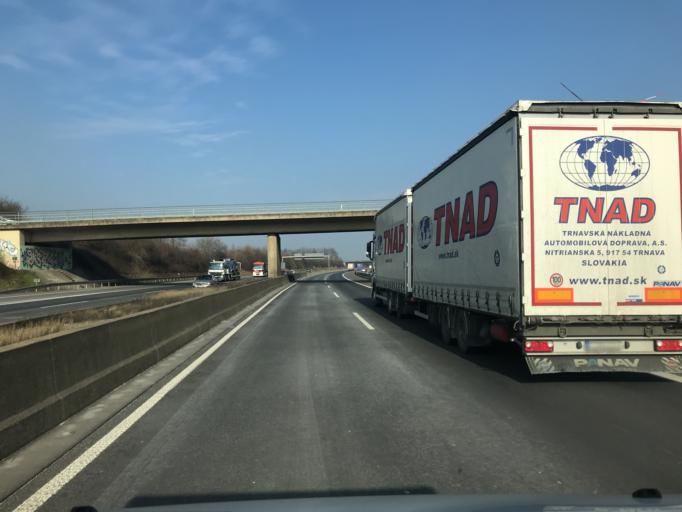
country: DE
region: North Rhine-Westphalia
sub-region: Regierungsbezirk Dusseldorf
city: Juchen
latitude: 51.0921
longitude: 6.4207
